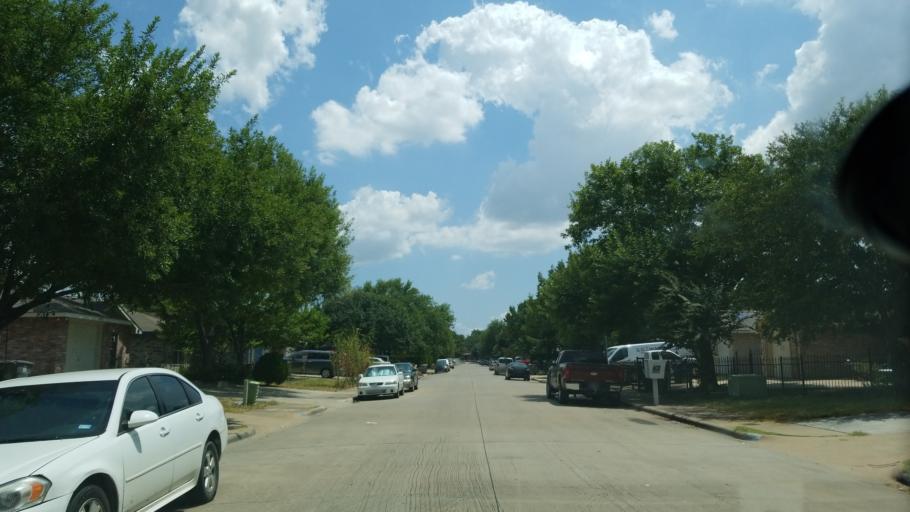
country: US
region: Texas
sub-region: Dallas County
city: Cockrell Hill
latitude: 32.7273
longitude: -96.8946
